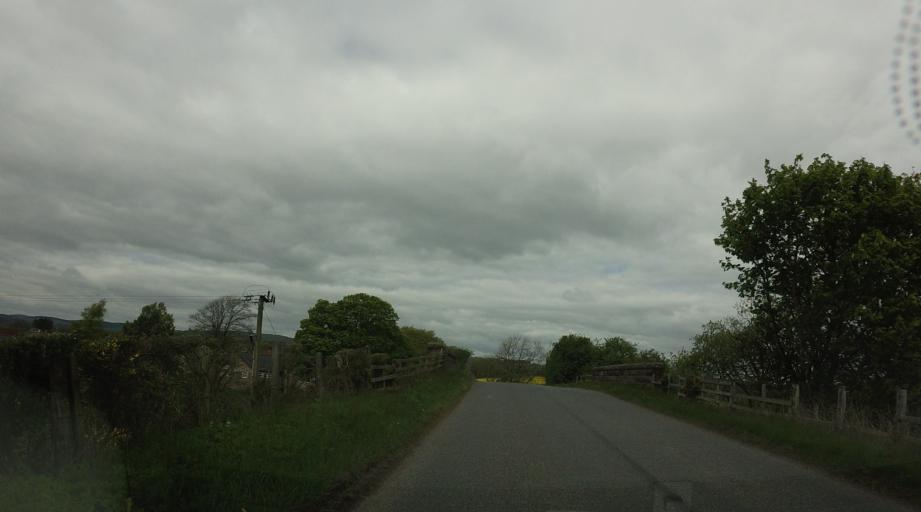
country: GB
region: Scotland
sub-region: Perth and Kinross
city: Milnathort
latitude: 56.2394
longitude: -3.3678
